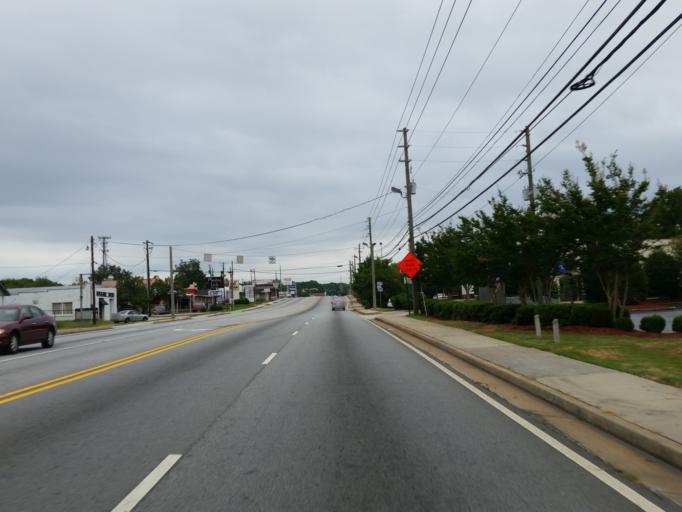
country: US
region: Georgia
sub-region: Cobb County
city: Mableton
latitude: 33.8187
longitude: -84.5805
